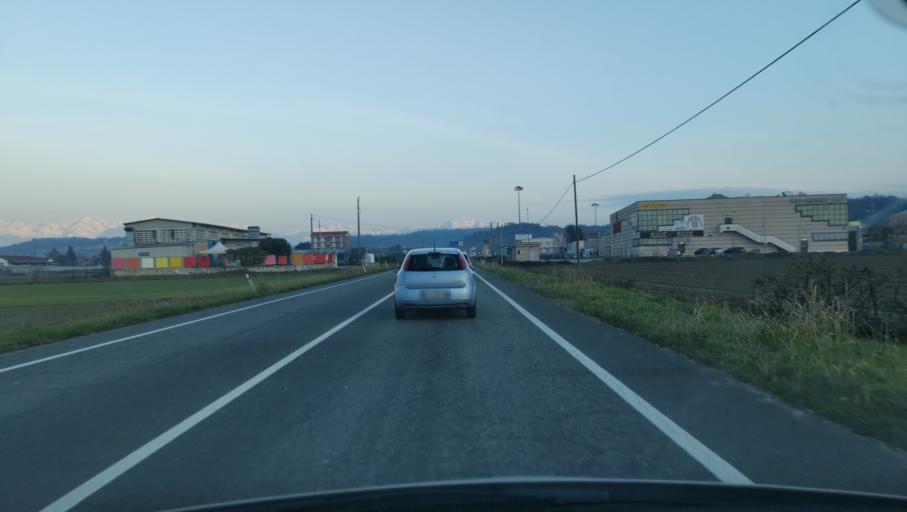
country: IT
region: Piedmont
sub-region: Provincia di Torino
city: Caluso
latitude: 45.3041
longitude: 7.8787
